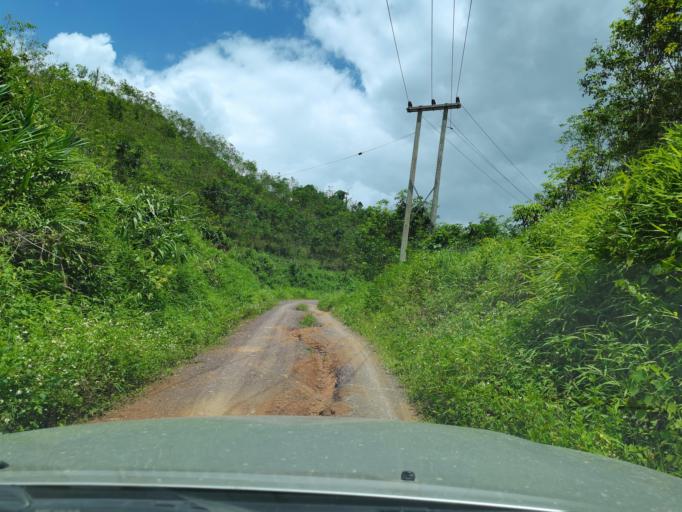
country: LA
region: Loungnamtha
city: Muang Long
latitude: 20.7190
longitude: 101.0138
